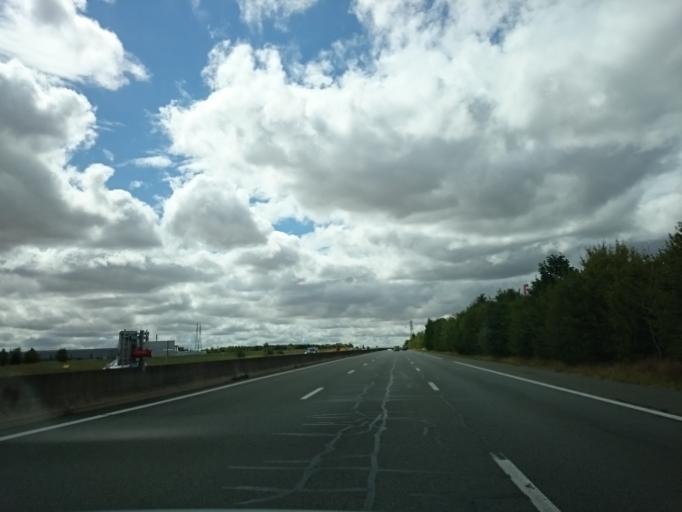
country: FR
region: Centre
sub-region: Departement d'Eure-et-Loir
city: Gasville-Oiseme
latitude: 48.4442
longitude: 1.5292
